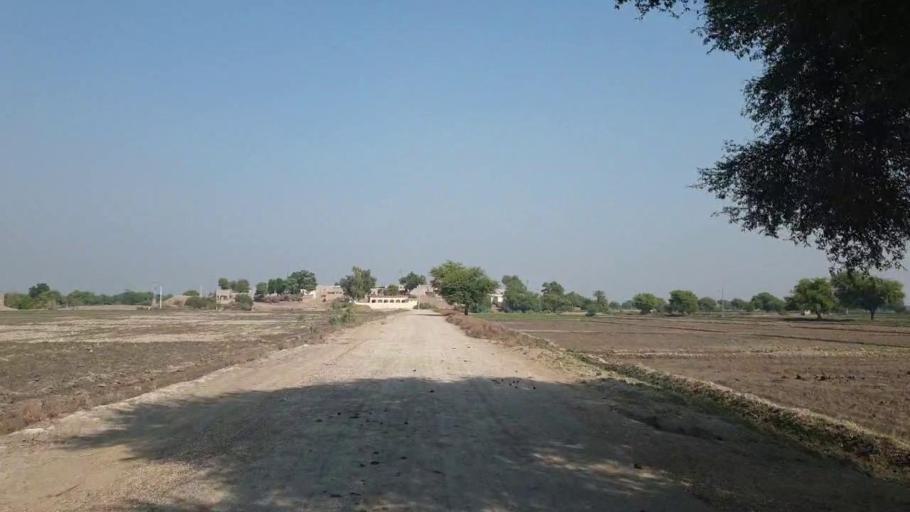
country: PK
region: Sindh
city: Sehwan
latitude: 26.4285
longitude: 67.7820
